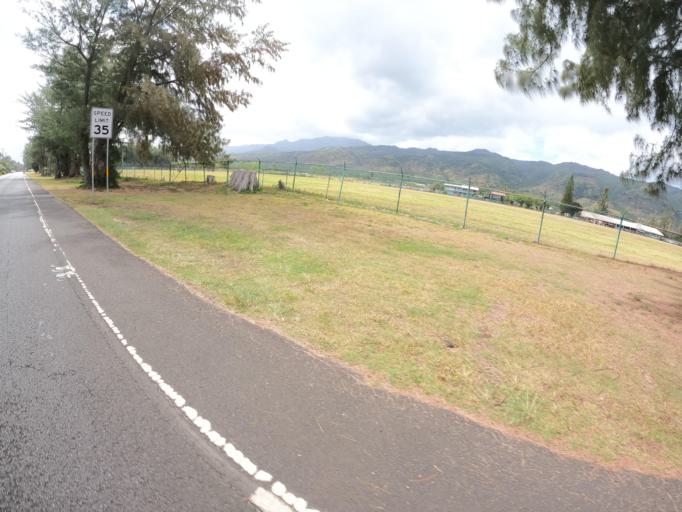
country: US
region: Hawaii
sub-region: Honolulu County
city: Mokuleia
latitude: 21.5802
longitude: -158.1823
